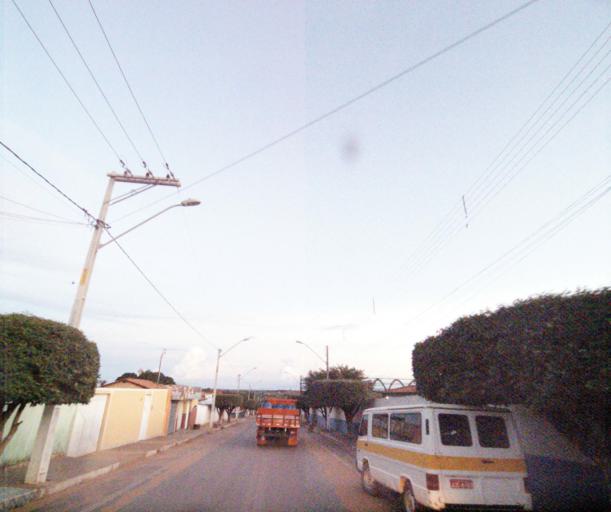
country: BR
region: Bahia
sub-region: Sao Felix Do Coribe
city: Santa Maria da Vitoria
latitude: -13.8284
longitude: -44.4570
